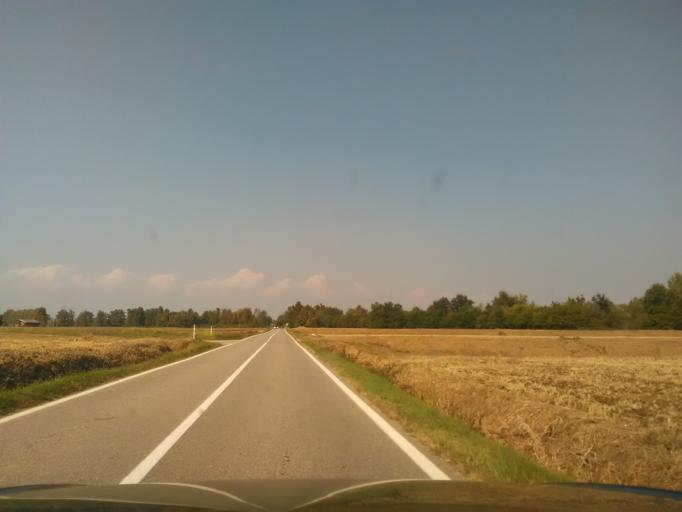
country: IT
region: Piedmont
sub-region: Provincia di Vercelli
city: Santhia
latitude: 45.4039
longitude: 8.1527
